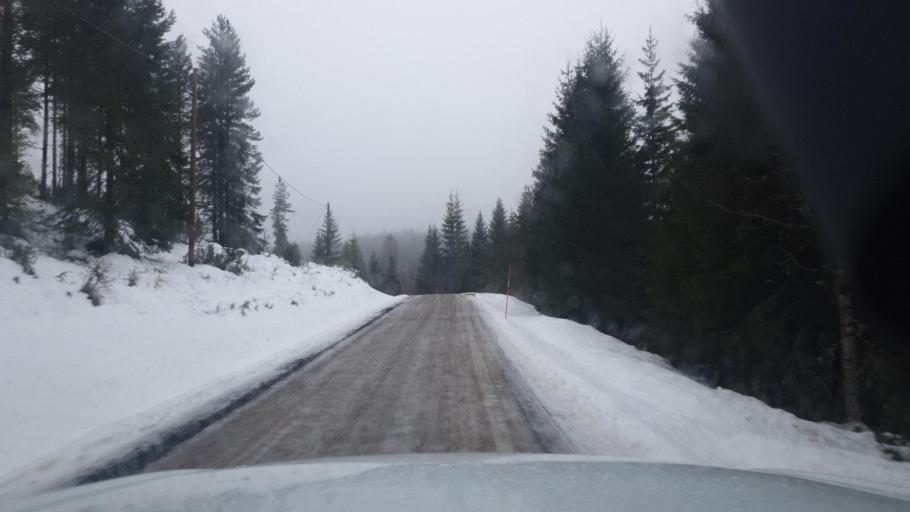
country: SE
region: Vaermland
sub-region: Eda Kommun
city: Charlottenberg
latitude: 60.1338
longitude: 12.5926
